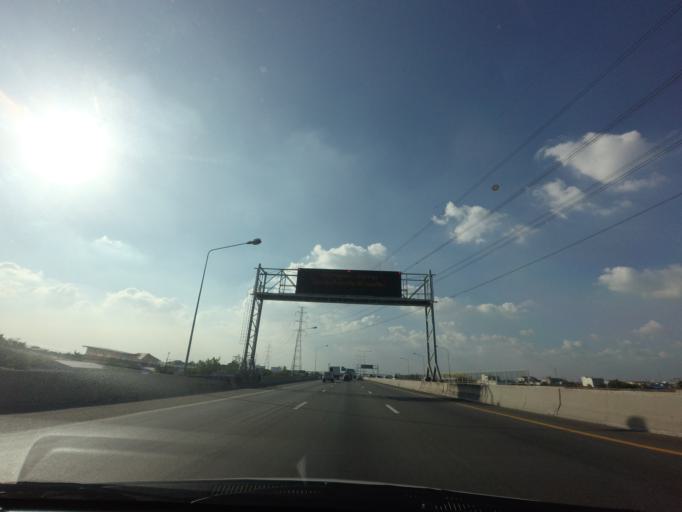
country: TH
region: Samut Prakan
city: Samut Prakan
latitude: 13.6226
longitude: 100.6037
